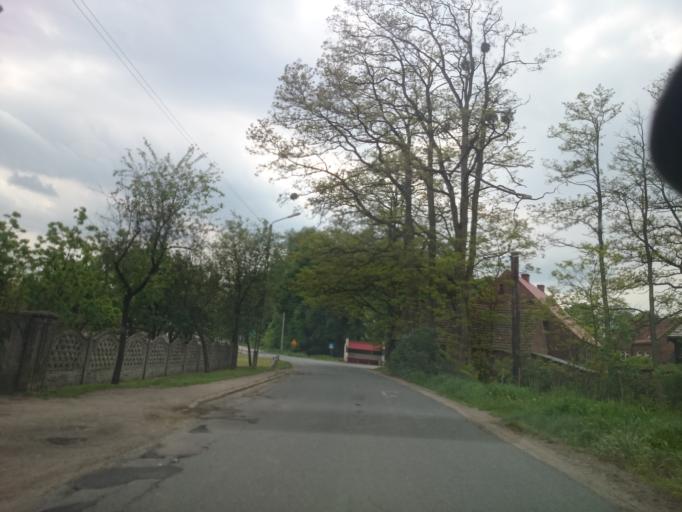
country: PL
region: Lower Silesian Voivodeship
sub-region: Powiat olesnicki
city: Dobroszyce
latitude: 51.3589
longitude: 17.2832
